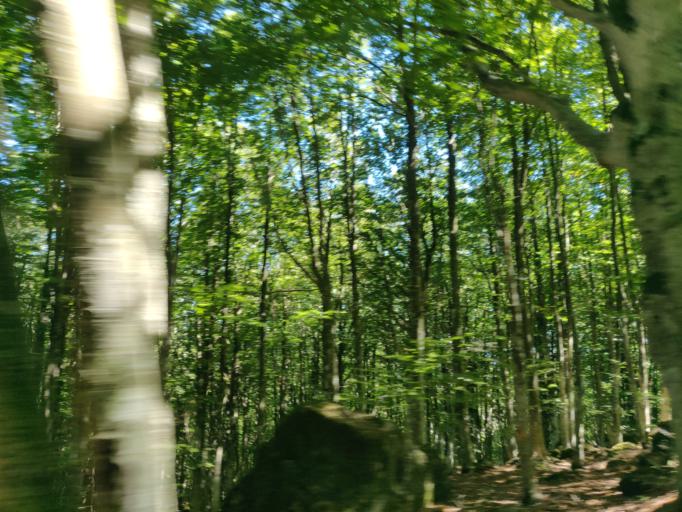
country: IT
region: Tuscany
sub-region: Provincia di Siena
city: Abbadia San Salvatore
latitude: 42.8912
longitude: 11.6327
